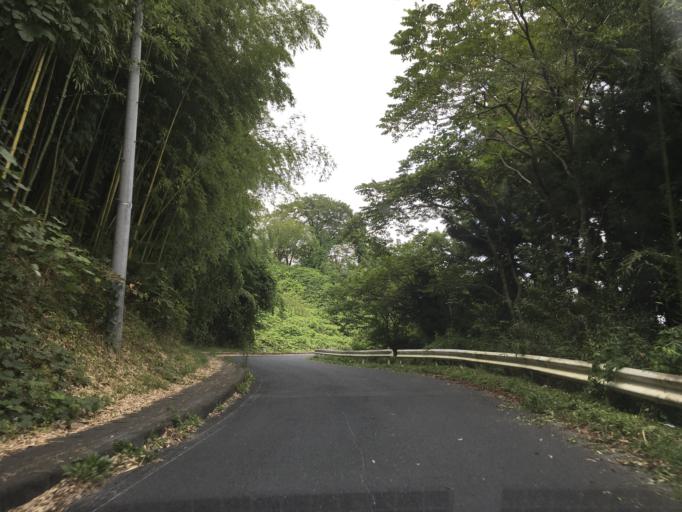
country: JP
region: Iwate
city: Ichinoseki
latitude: 38.9929
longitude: 141.2480
